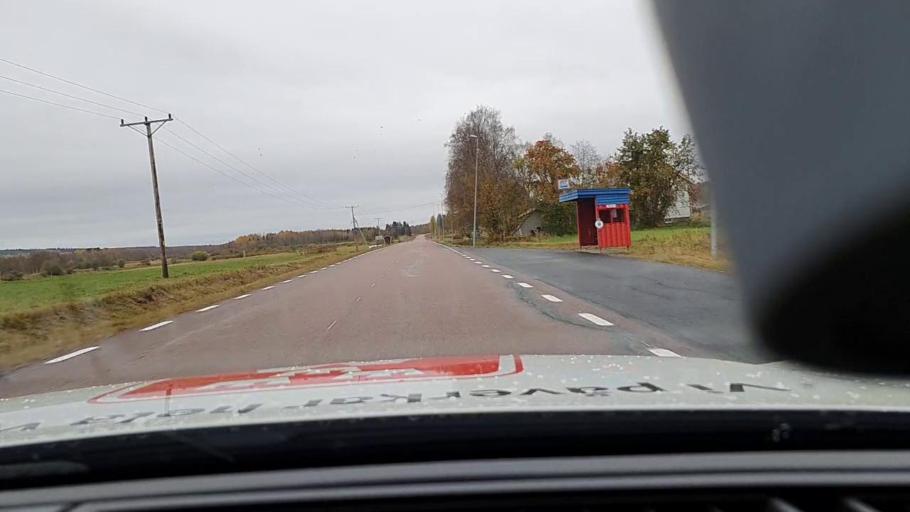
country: FI
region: Lapland
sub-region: Torniolaakso
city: Ylitornio
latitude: 66.1345
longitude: 23.9049
